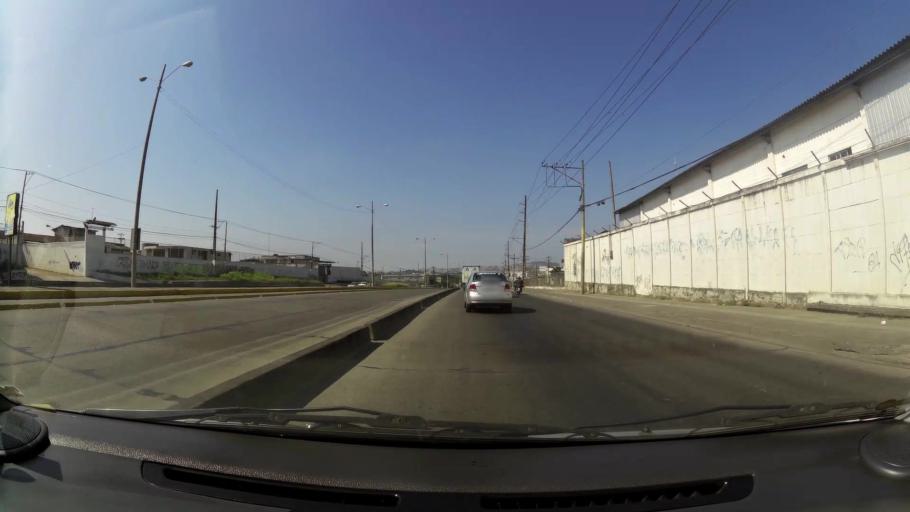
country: EC
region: Guayas
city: Santa Lucia
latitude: -2.1082
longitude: -79.9344
